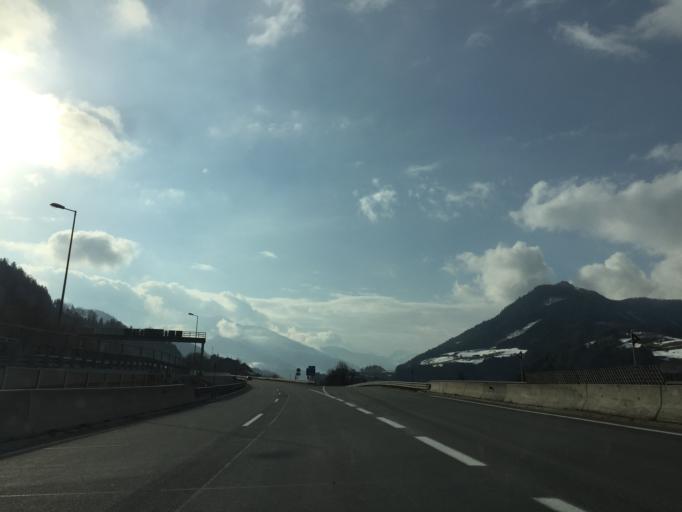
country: AT
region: Salzburg
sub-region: Politischer Bezirk Sankt Johann im Pongau
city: Pfarrwerfen
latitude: 47.4714
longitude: 13.1985
